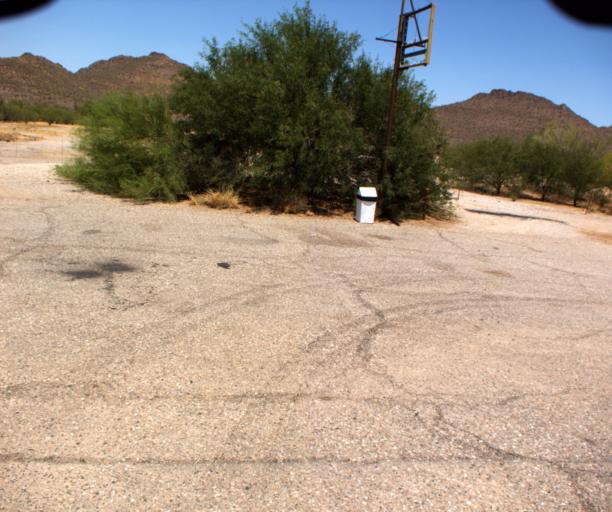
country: US
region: Arizona
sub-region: Pinal County
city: Gold Camp
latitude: 33.2586
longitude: -111.3363
